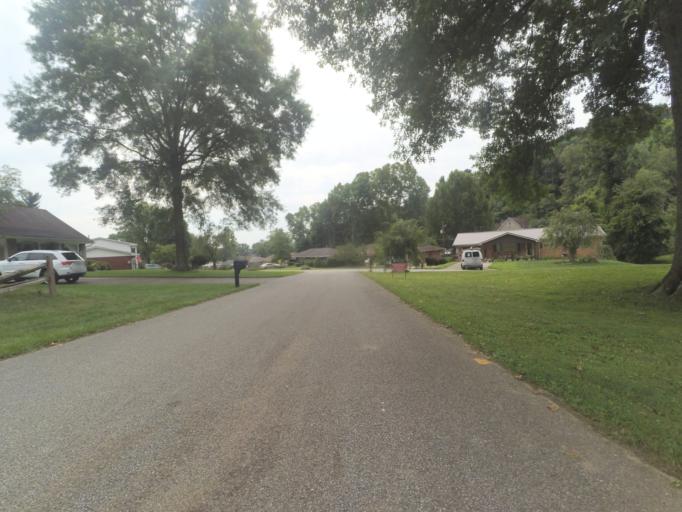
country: US
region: West Virginia
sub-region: Cabell County
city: Huntington
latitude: 38.4364
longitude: -82.4693
